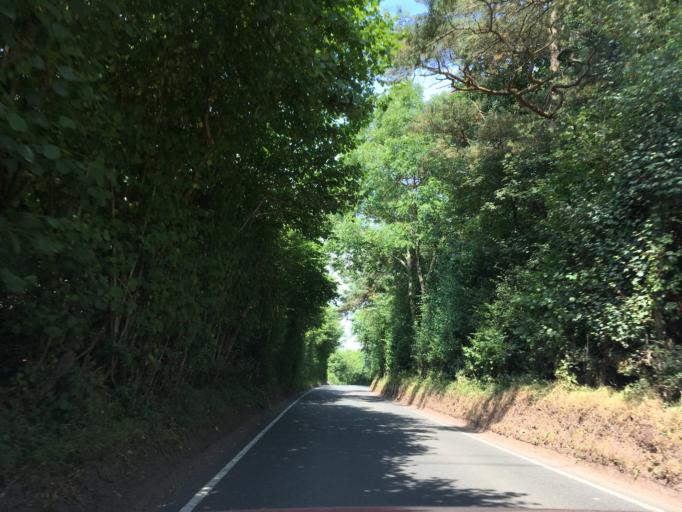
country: GB
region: Wales
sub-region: Newport
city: Langstone
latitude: 51.6096
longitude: -2.9315
